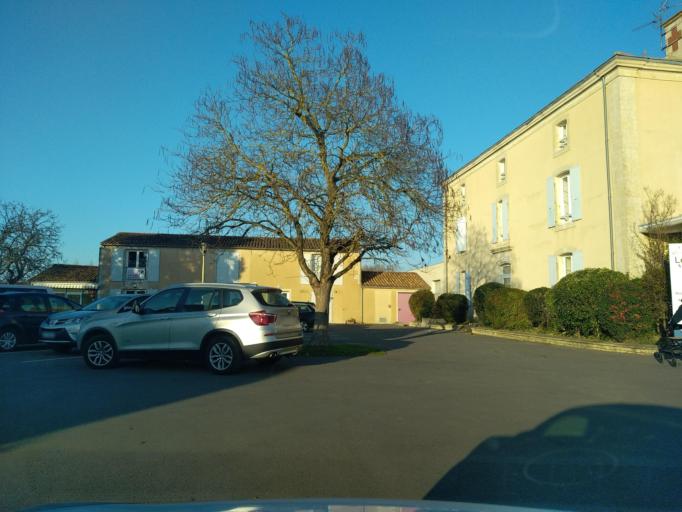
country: FR
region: Pays de la Loire
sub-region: Departement de la Vendee
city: Maillezais
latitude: 46.3423
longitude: -0.7875
